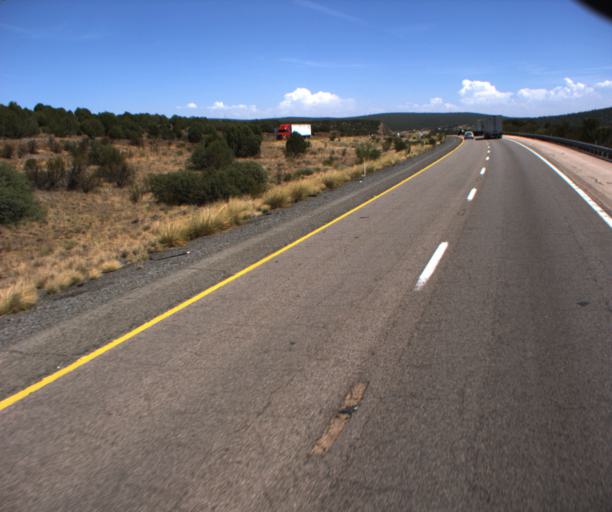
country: US
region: Arizona
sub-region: Mohave County
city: Peach Springs
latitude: 35.1925
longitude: -113.3103
